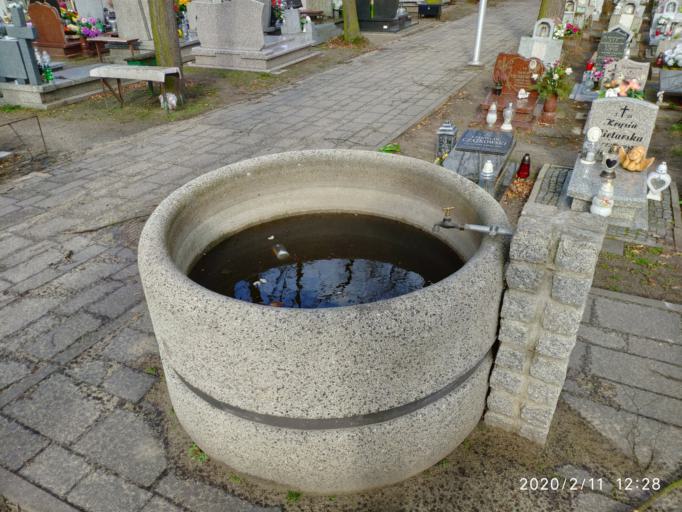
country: PL
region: Lubusz
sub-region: Powiat nowosolski
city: Nowa Sol
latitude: 51.8089
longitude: 15.7232
